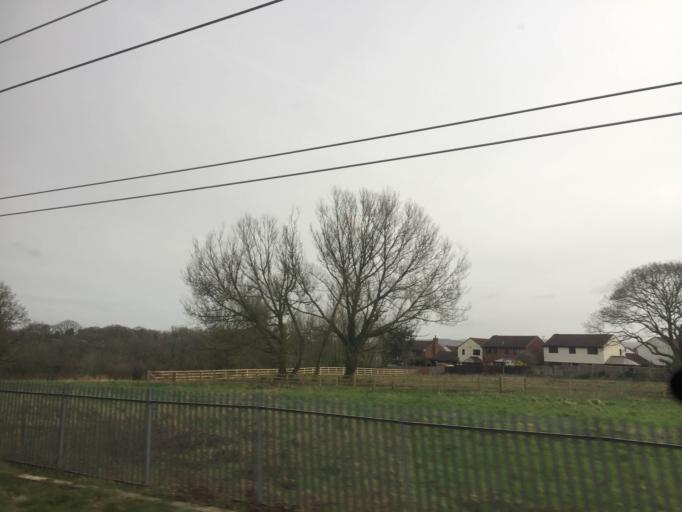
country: GB
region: England
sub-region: Lancashire
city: Coppull
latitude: 53.6304
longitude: -2.6620
